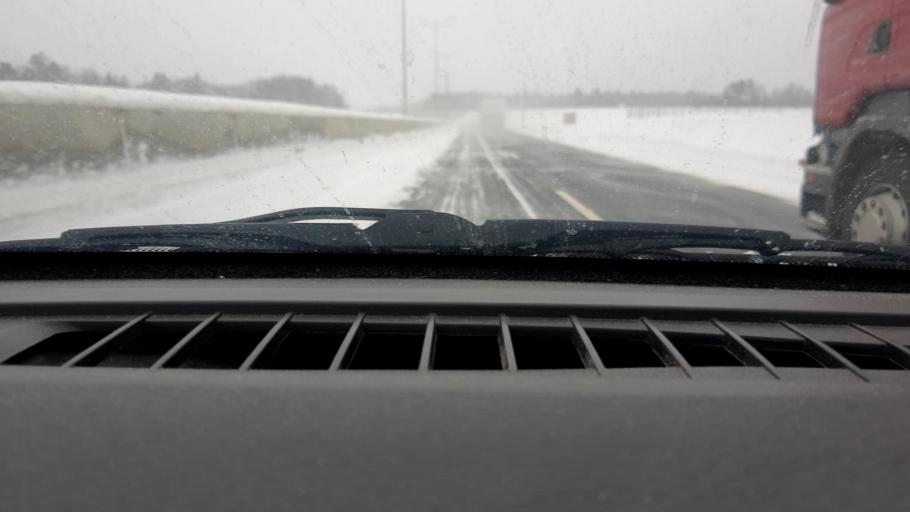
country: RU
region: Moskovskaya
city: Krasnoarmeysk
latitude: 56.0704
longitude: 38.0817
